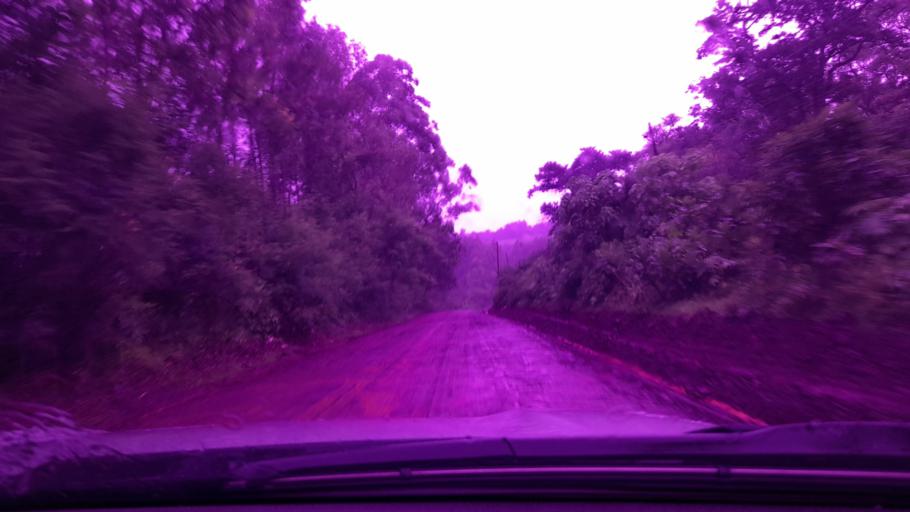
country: ET
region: Oromiya
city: Metu
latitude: 8.3294
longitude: 35.6037
